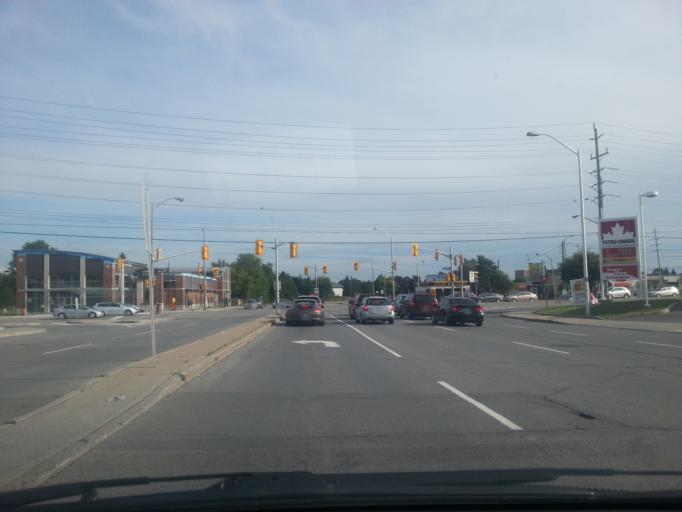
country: CA
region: Ontario
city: Ottawa
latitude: 45.4480
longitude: -75.5946
